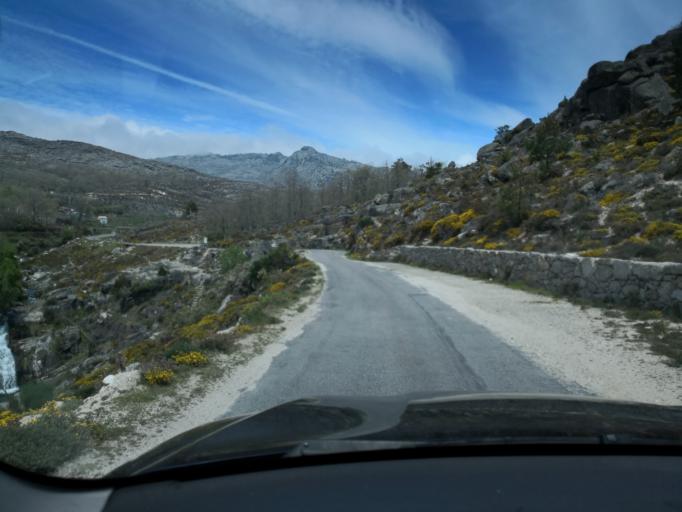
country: PT
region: Vila Real
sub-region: Vila Real
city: Vila Real
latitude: 41.3244
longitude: -7.7988
